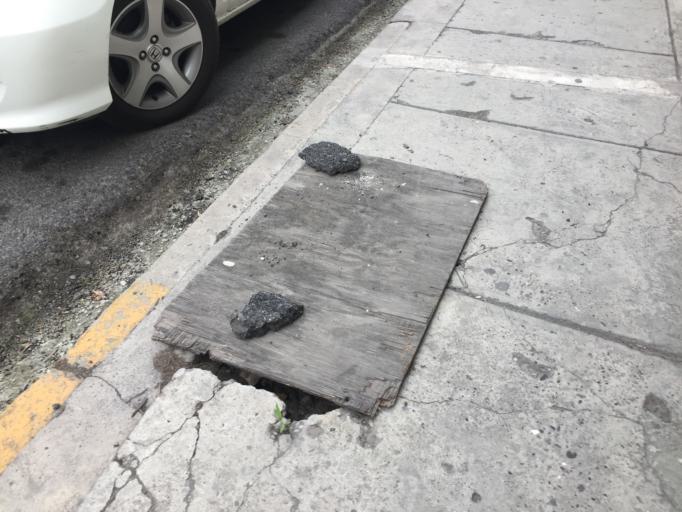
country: MX
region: Nuevo Leon
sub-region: Monterrey
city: Monterrey
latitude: 25.6816
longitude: -100.3071
